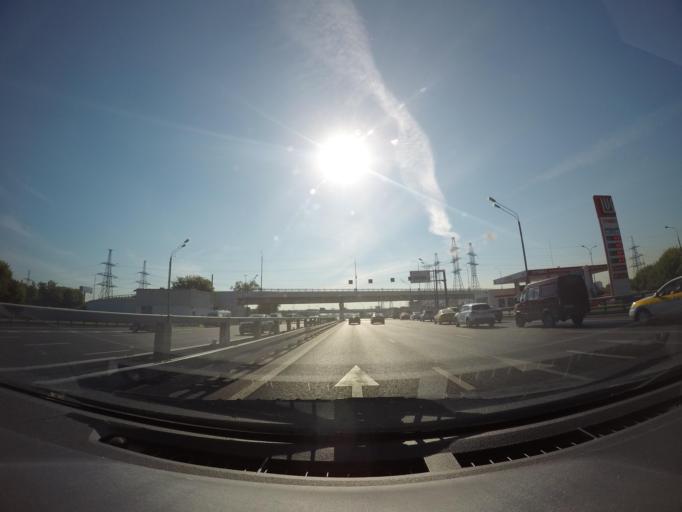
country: RU
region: Moscow
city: Veshnyaki
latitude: 55.7087
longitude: 37.8309
